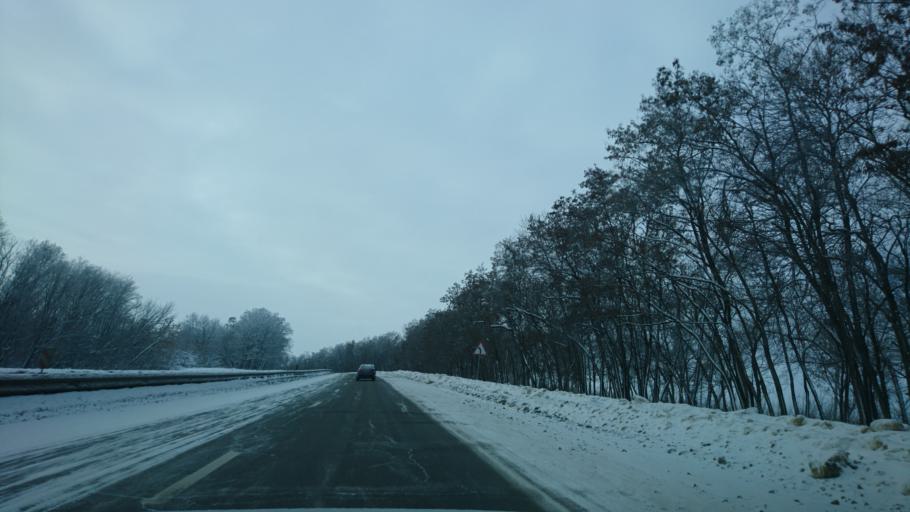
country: RU
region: Belgorod
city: Mayskiy
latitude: 50.4846
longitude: 36.4095
